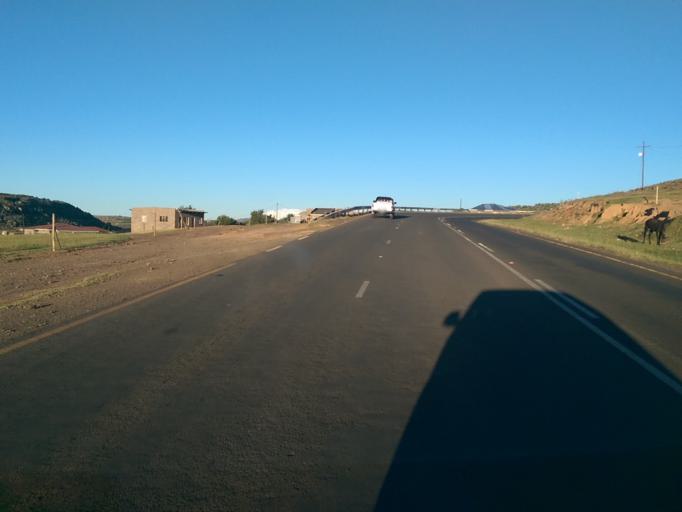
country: LS
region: Maseru
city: Maseru
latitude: -29.4024
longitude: 27.5721
